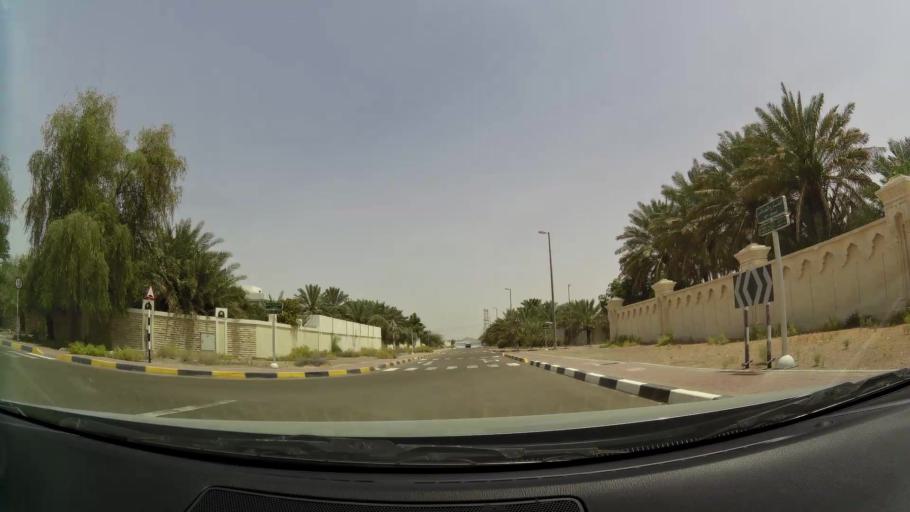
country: AE
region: Abu Dhabi
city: Al Ain
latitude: 24.1888
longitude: 55.6798
